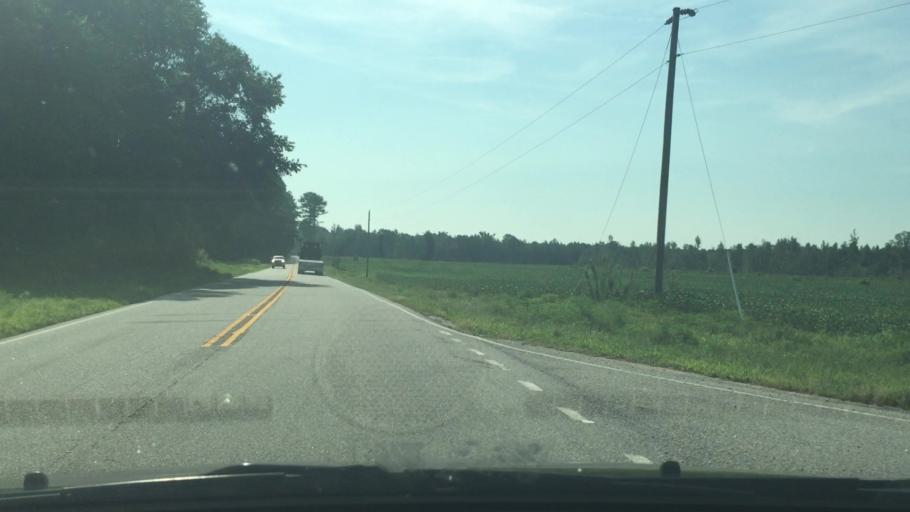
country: US
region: Virginia
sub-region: Sussex County
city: Sussex
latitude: 36.9915
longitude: -77.2565
